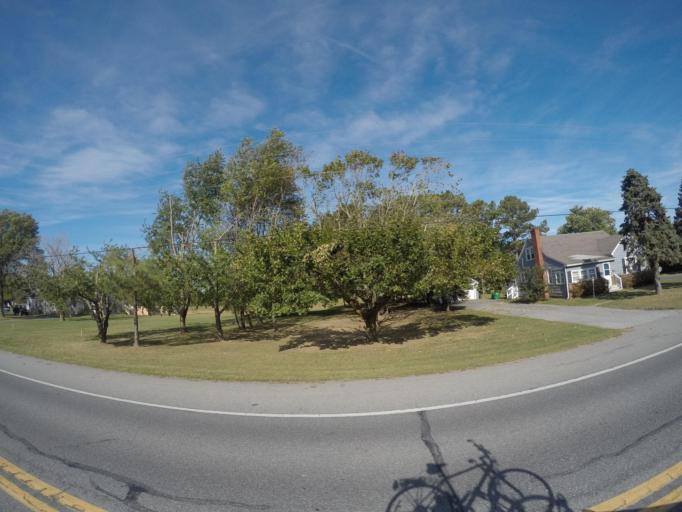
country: US
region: Delaware
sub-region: Sussex County
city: Milton
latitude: 38.8031
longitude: -75.2747
